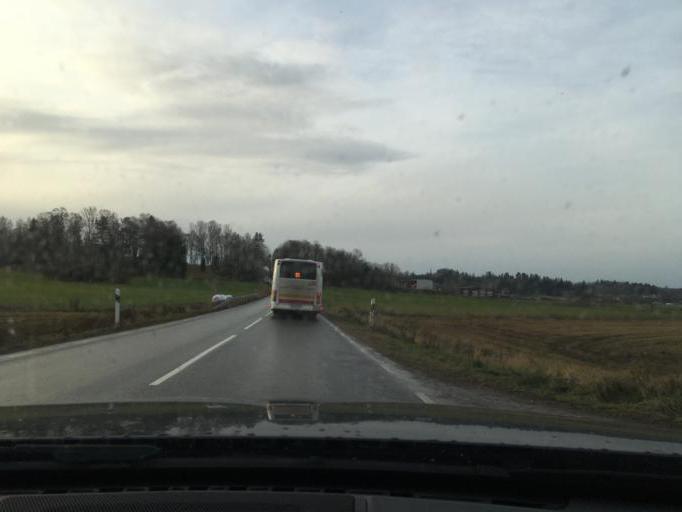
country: SE
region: Joenkoeping
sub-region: Jonkopings Kommun
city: Graenna
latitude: 57.9319
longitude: 14.4009
